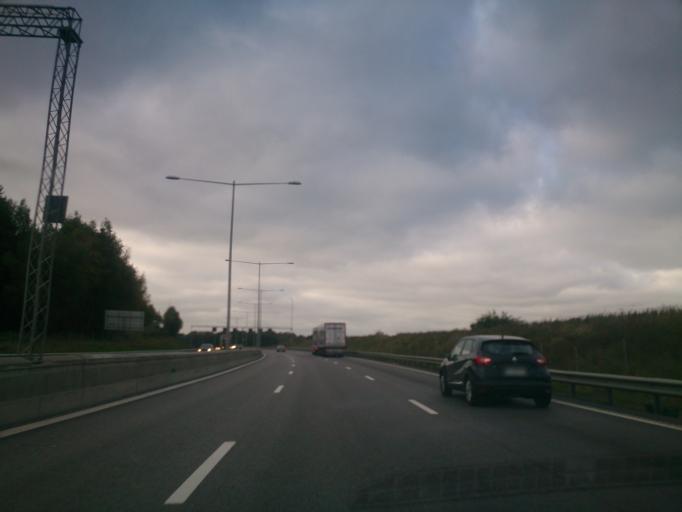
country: SE
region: Stockholm
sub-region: Botkyrka Kommun
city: Eriksberg
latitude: 59.2375
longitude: 17.8172
